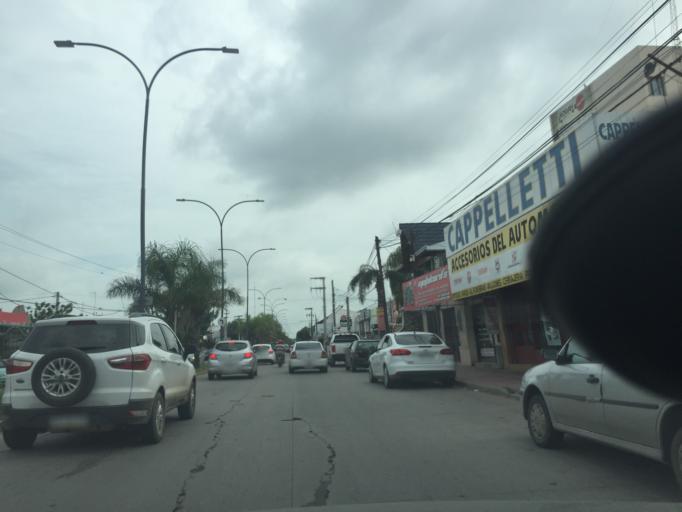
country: AR
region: Cordoba
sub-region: Departamento de Capital
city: Cordoba
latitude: -31.4458
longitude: -64.1985
